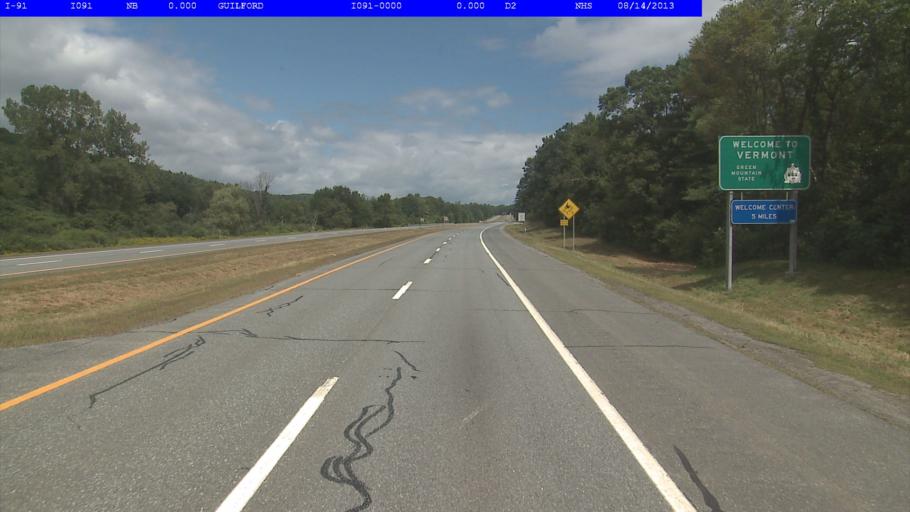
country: US
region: Massachusetts
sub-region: Franklin County
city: Bernardston
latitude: 42.7301
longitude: -72.5699
